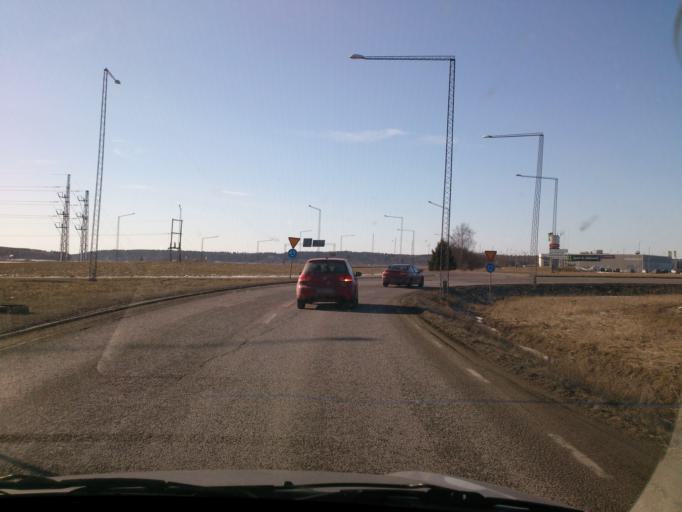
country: SE
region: Uppsala
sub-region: Uppsala Kommun
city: Saevja
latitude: 59.8457
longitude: 17.7018
